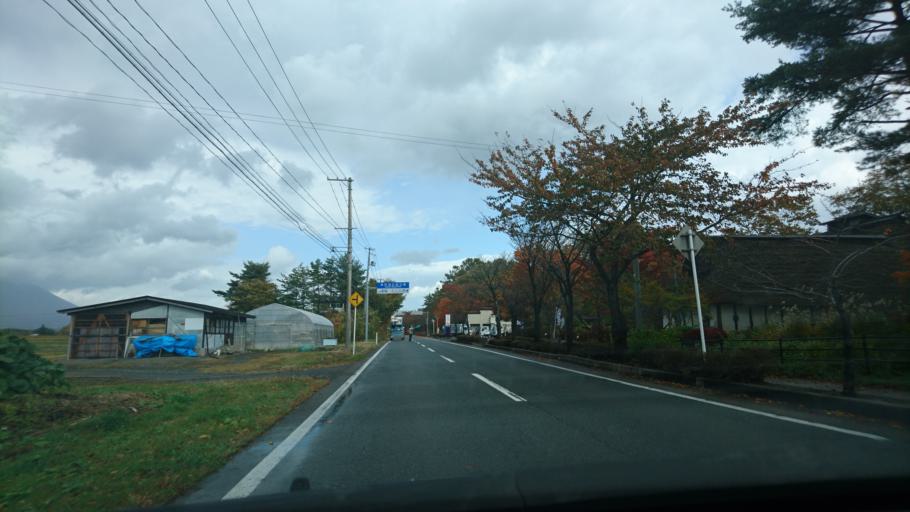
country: JP
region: Iwate
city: Shizukuishi
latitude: 39.6865
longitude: 141.0221
